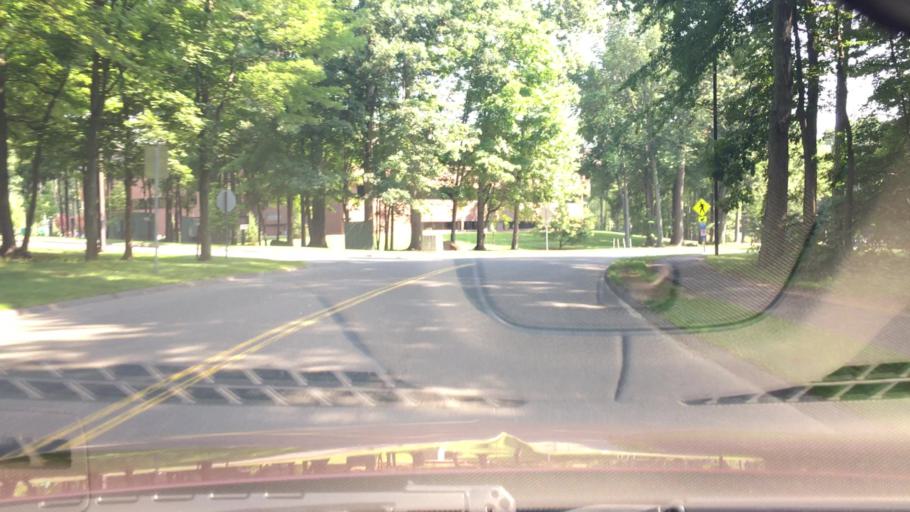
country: US
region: Connecticut
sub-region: Hartford County
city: Farmington
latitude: 41.7111
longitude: -72.8045
